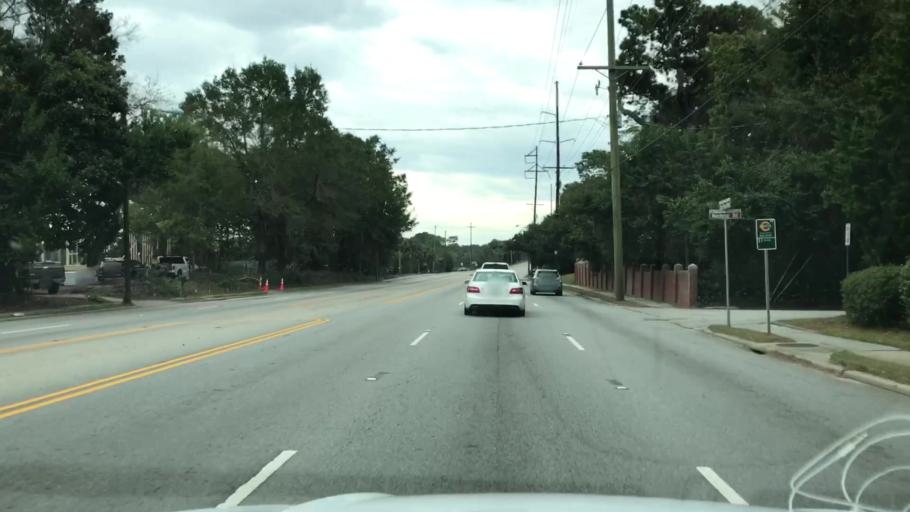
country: US
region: South Carolina
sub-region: Charleston County
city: Charleston
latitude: 32.7714
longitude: -79.9737
